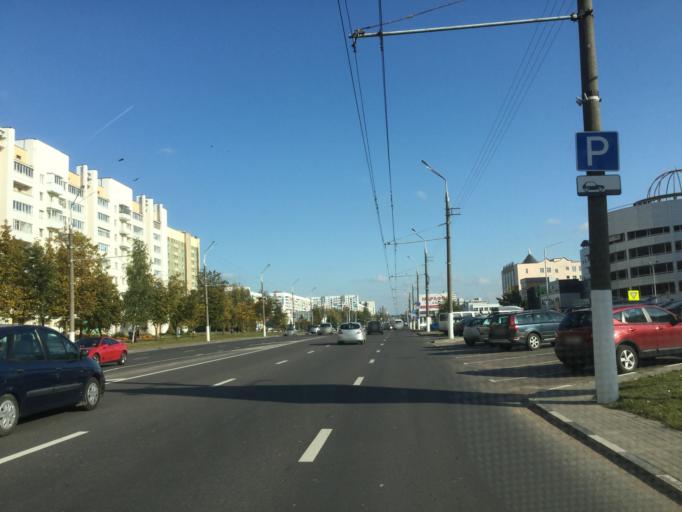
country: BY
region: Vitebsk
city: Vitebsk
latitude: 55.1709
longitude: 30.2203
